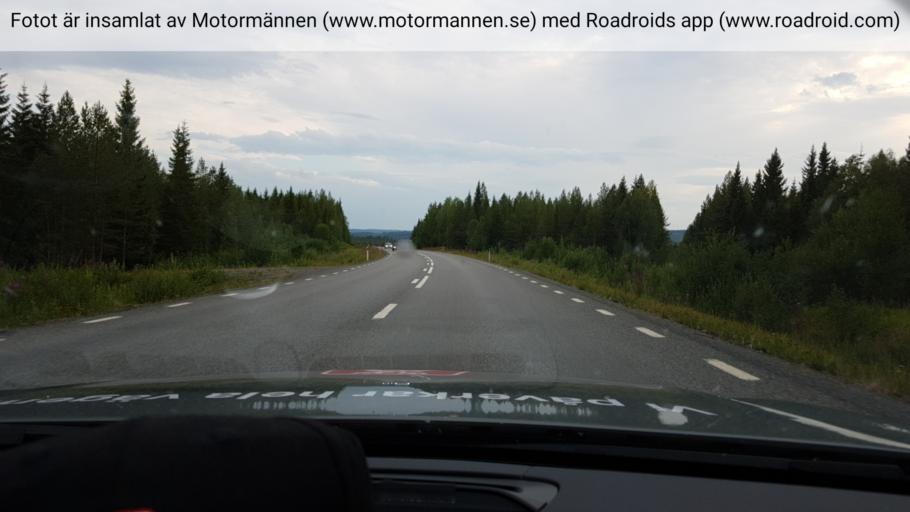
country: SE
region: Jaemtland
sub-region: OEstersunds Kommun
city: Lit
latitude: 63.3861
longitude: 14.8941
